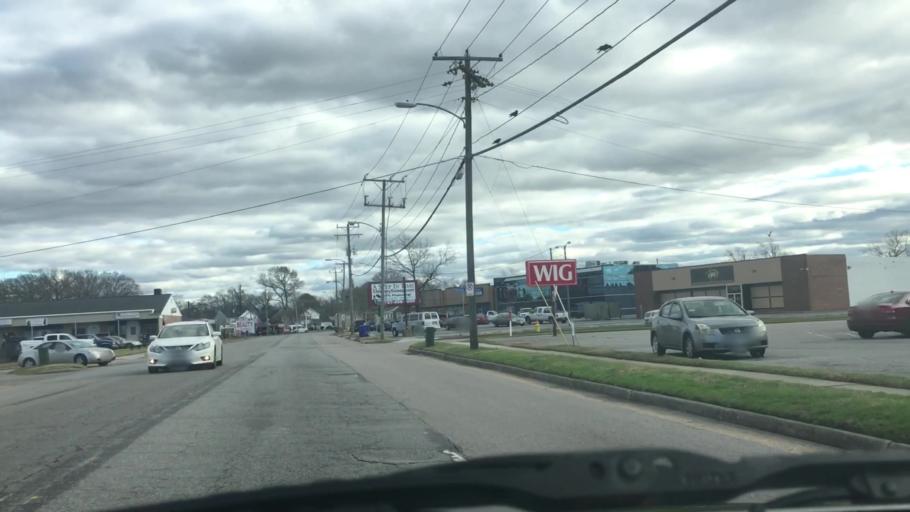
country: US
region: Virginia
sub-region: City of Norfolk
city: Norfolk
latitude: 36.9141
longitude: -76.2494
